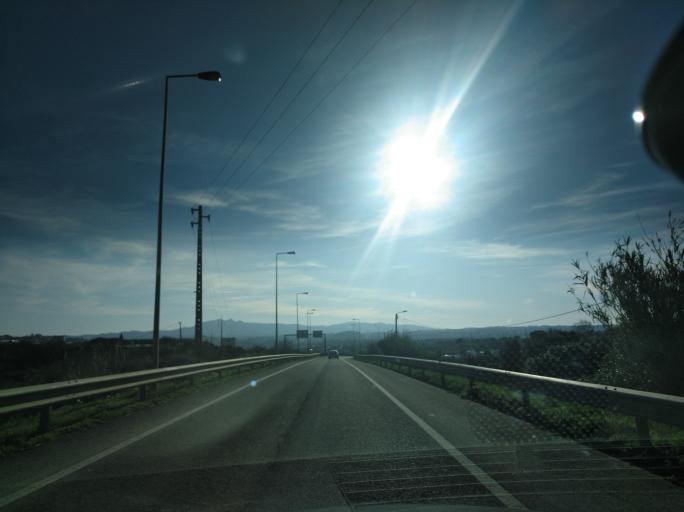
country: PT
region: Lisbon
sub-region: Sintra
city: Pero Pinheiro
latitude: 38.8705
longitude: -9.3311
